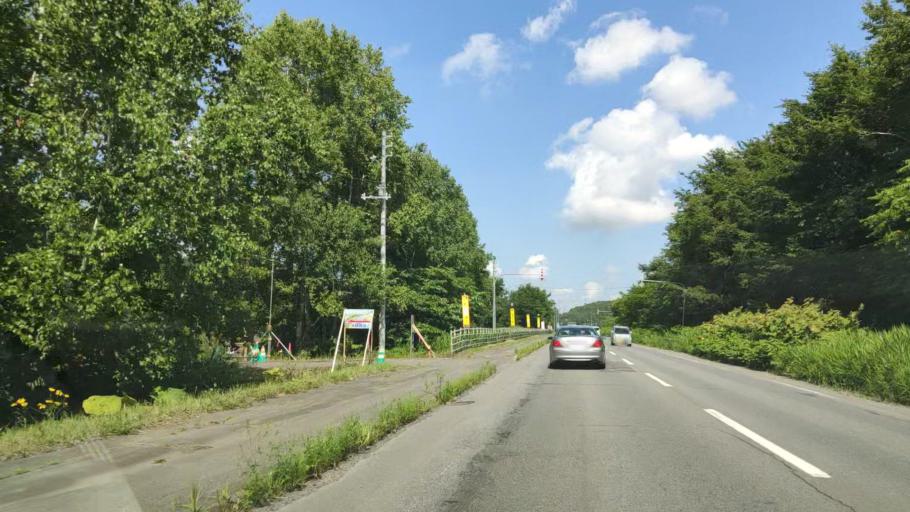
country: JP
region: Hokkaido
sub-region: Asahikawa-shi
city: Asahikawa
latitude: 43.6229
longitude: 142.4682
